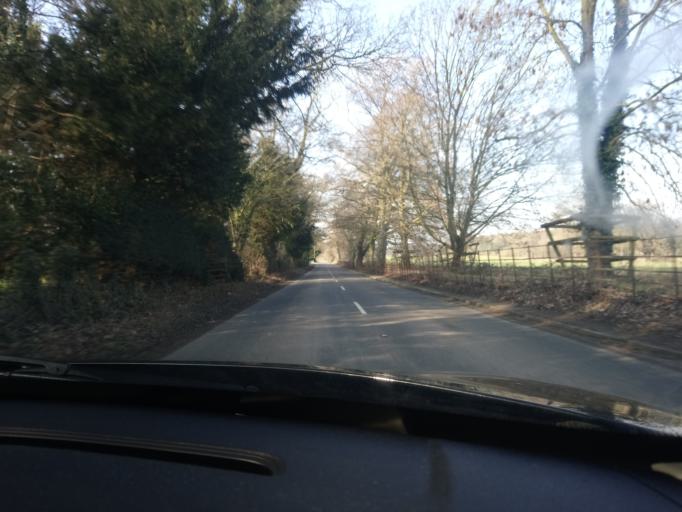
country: GB
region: England
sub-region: Shropshire
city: Shrewsbury
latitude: 52.7258
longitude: -2.7706
